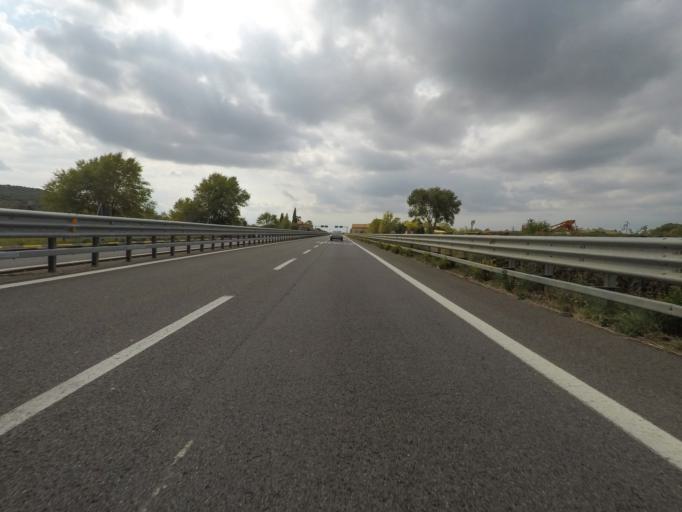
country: IT
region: Tuscany
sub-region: Provincia di Grosseto
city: Bagno Roselle
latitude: 42.8263
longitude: 11.1374
